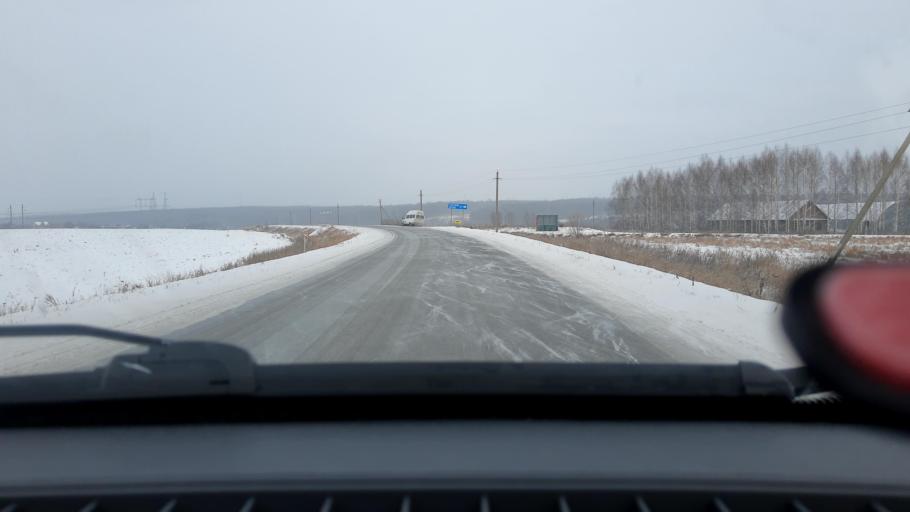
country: RU
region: Bashkortostan
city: Iglino
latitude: 54.7519
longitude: 56.4000
